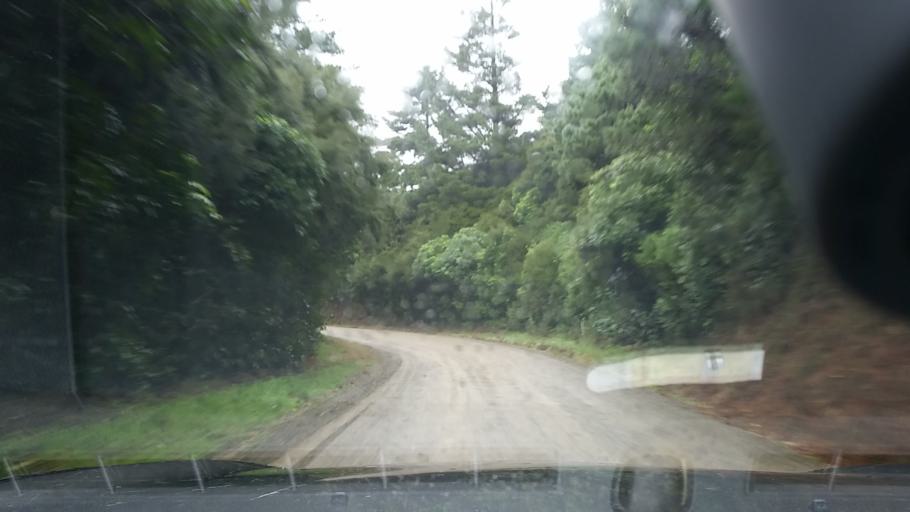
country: NZ
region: Marlborough
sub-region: Marlborough District
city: Picton
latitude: -41.3752
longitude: 174.0639
